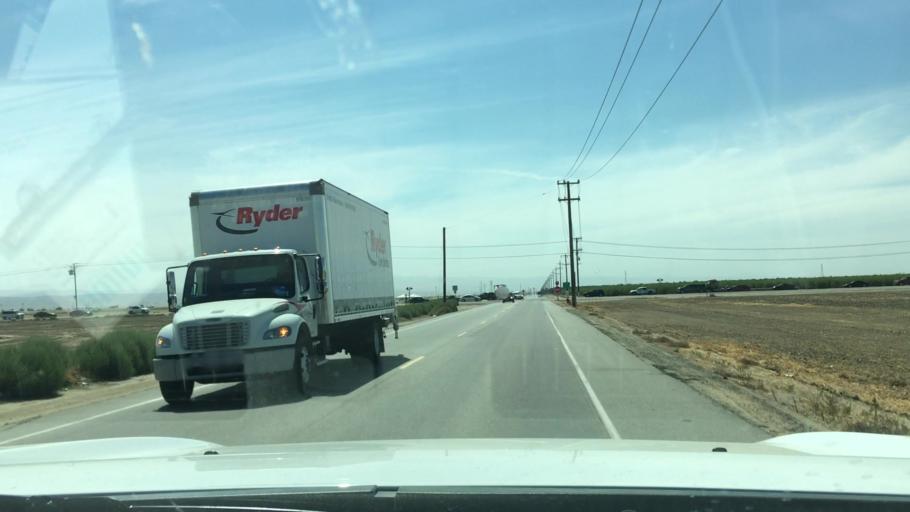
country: US
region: California
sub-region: Kern County
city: Rosedale
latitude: 35.3544
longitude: -119.2501
